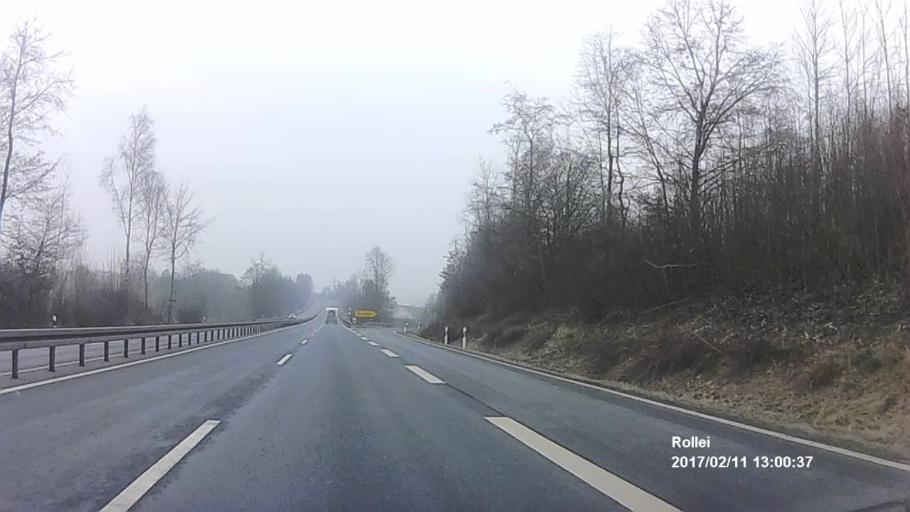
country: DE
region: Lower Saxony
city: Gittelde
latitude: 51.8184
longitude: 10.1895
